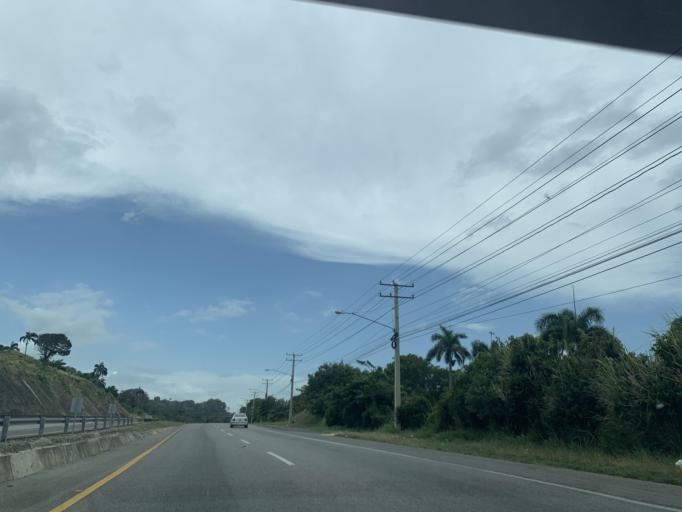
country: DO
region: Puerto Plata
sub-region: Puerto Plata
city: Puerto Plata
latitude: 19.8279
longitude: -70.7521
